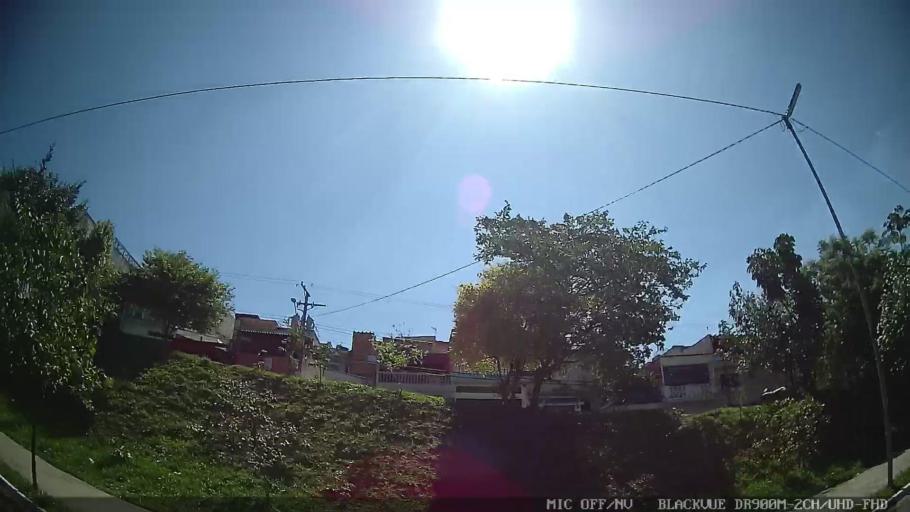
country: BR
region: Sao Paulo
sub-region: Sao Caetano Do Sul
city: Sao Caetano do Sul
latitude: -23.5931
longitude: -46.5069
